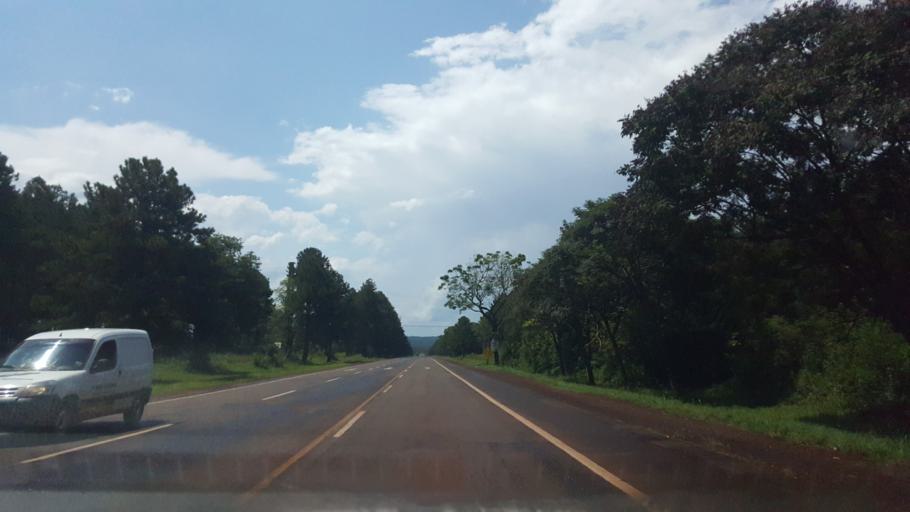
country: AR
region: Misiones
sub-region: Departamento de Eldorado
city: Eldorado
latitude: -26.3829
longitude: -54.6280
